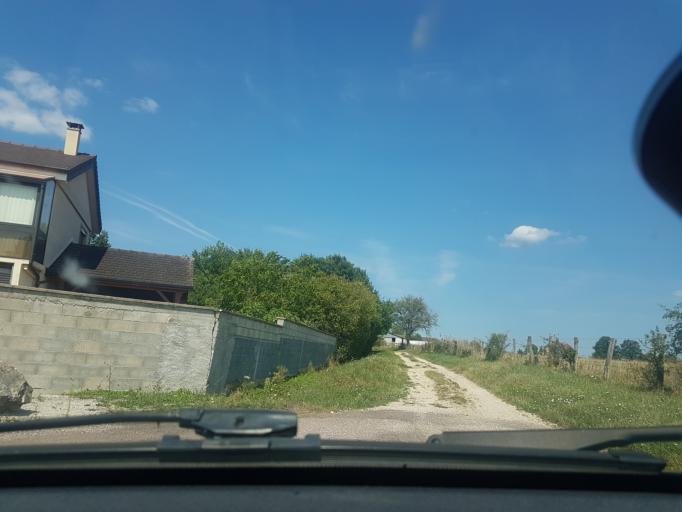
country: FR
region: Bourgogne
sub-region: Departement de Saone-et-Loire
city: Chagny
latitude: 46.9001
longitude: 4.7695
